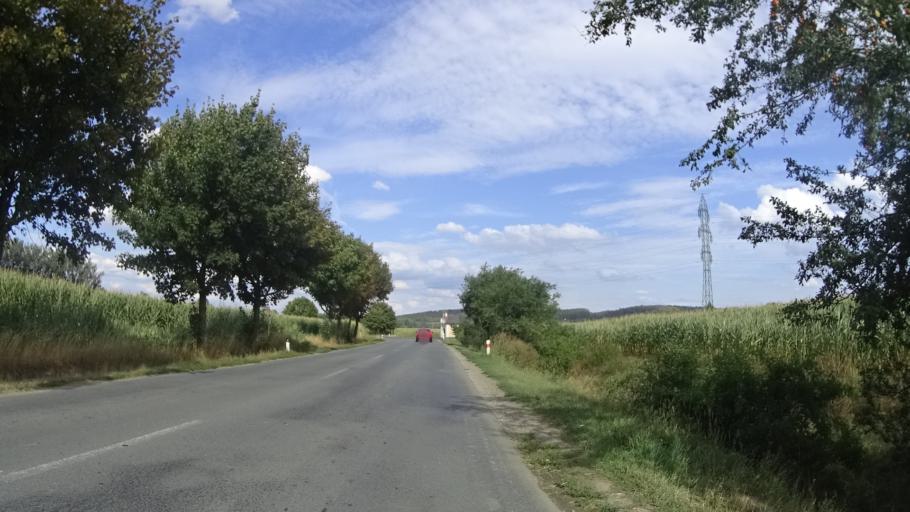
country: CZ
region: Olomoucky
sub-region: Okres Sumperk
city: Mohelnice
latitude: 49.7787
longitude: 16.9454
